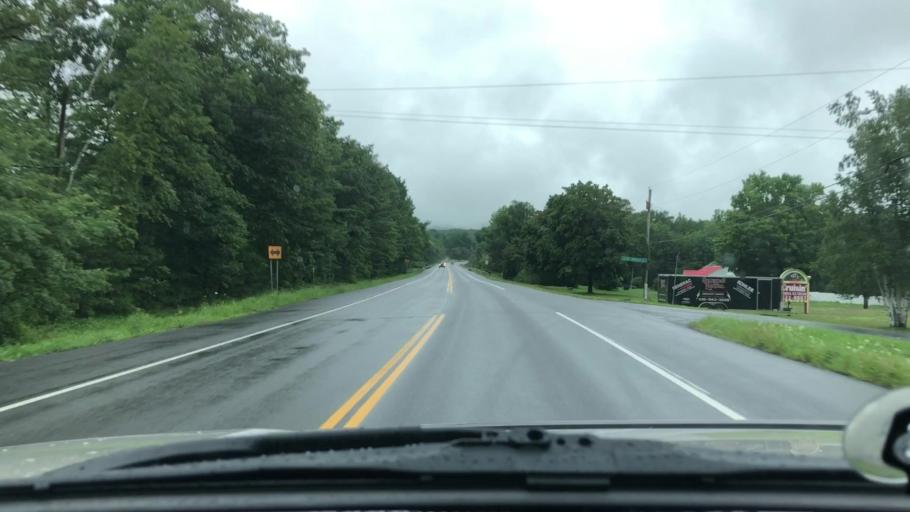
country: US
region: New York
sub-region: Greene County
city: Cairo
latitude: 42.3201
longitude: -74.0826
